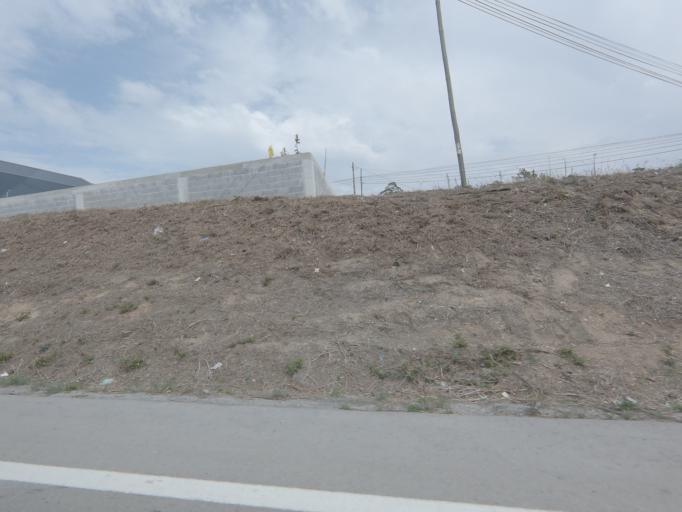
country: PT
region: Leiria
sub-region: Leiria
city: Caranguejeira
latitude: 39.8214
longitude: -8.7272
